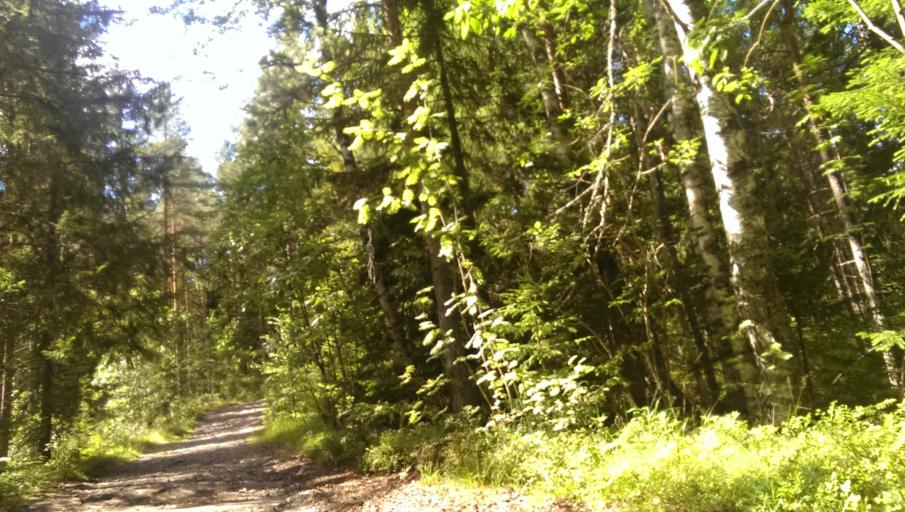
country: NO
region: Buskerud
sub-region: Kongsberg
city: Kongsberg
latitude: 59.6679
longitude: 9.6130
